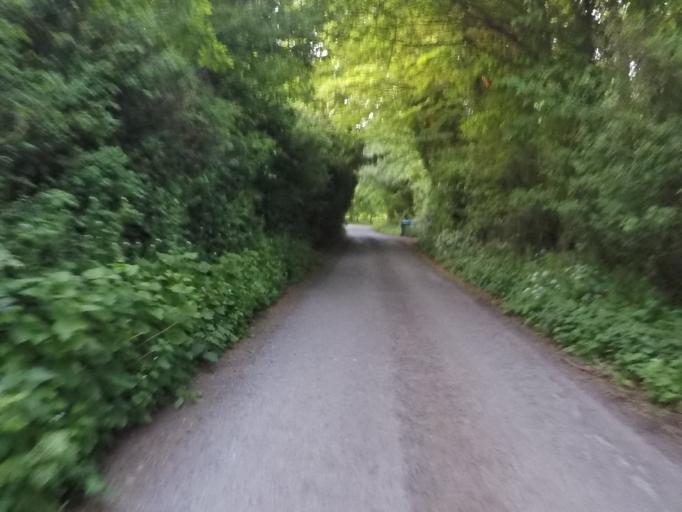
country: GB
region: England
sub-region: Oxfordshire
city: North Leigh
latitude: 51.8360
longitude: -1.4619
